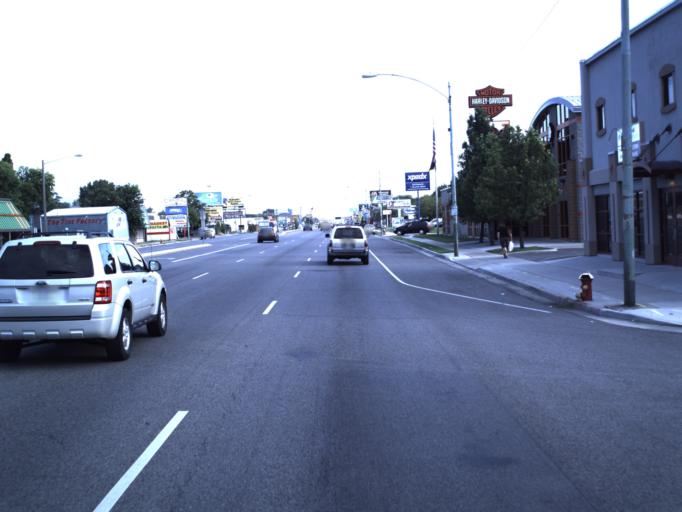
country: US
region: Utah
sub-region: Salt Lake County
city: South Salt Lake
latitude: 40.7083
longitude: -111.8884
